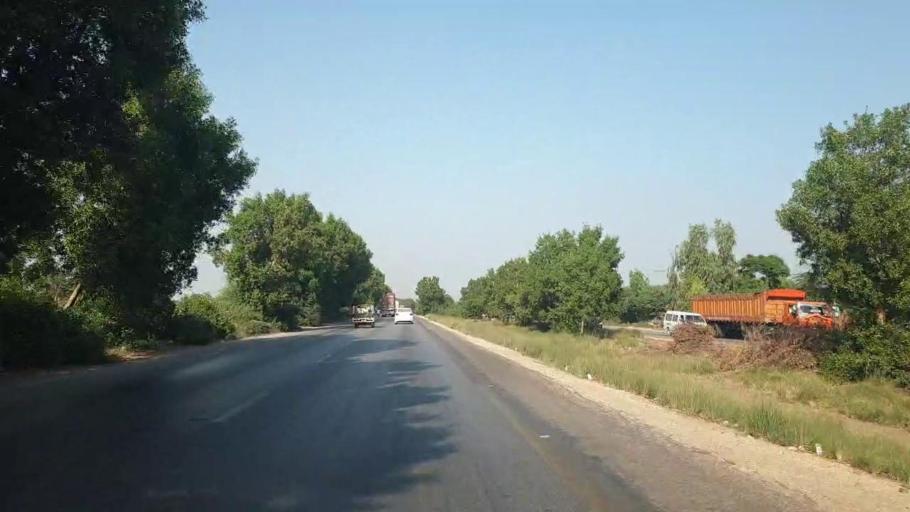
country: PK
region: Sindh
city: Matiari
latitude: 25.5053
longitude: 68.4265
